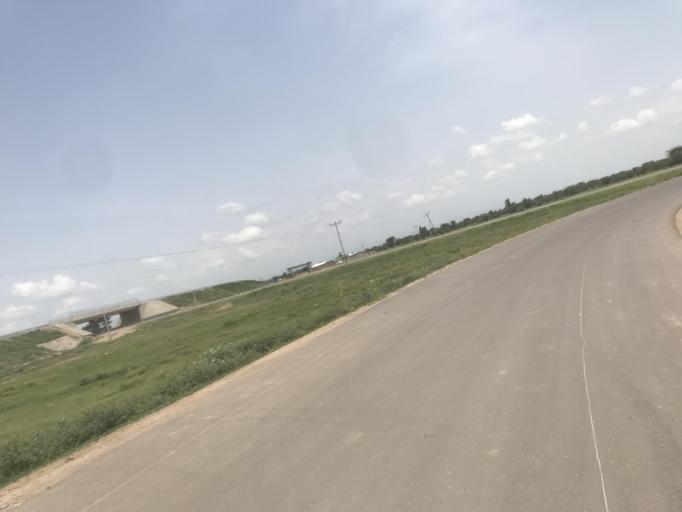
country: ET
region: Oromiya
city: Mojo
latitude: 8.3022
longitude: 38.9383
